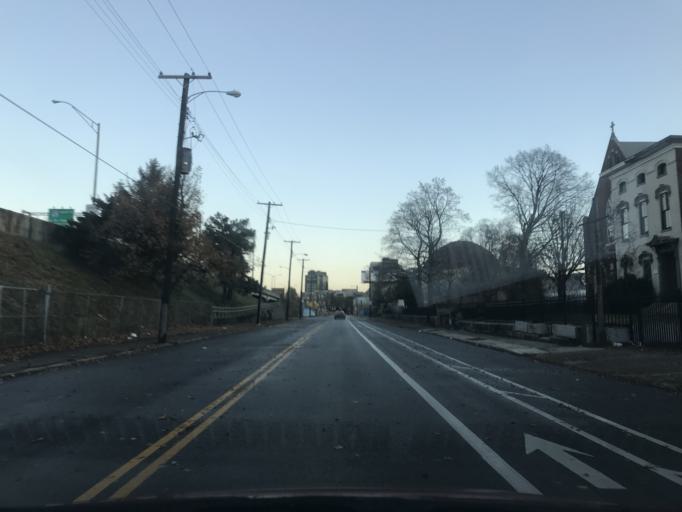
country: US
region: Kentucky
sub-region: Jefferson County
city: Louisville
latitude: 38.2419
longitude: -85.7524
